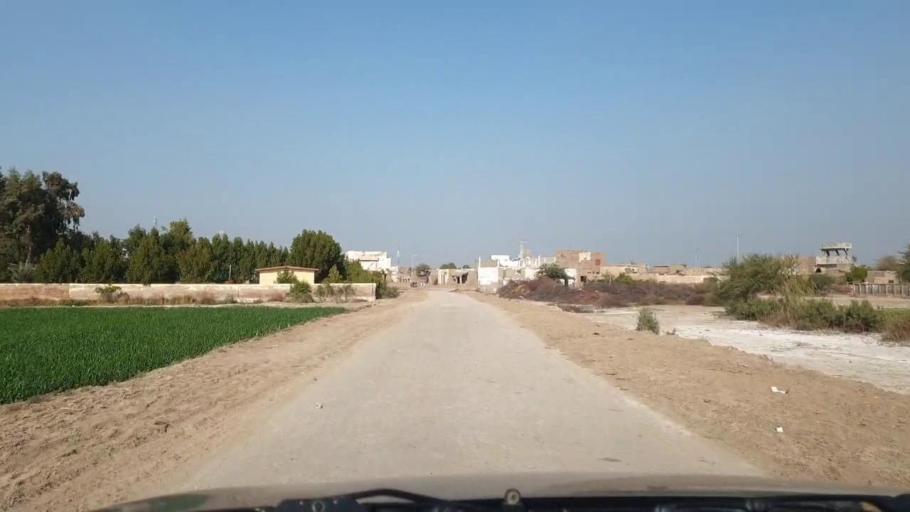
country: PK
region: Sindh
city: Jhol
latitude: 25.9486
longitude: 68.8856
